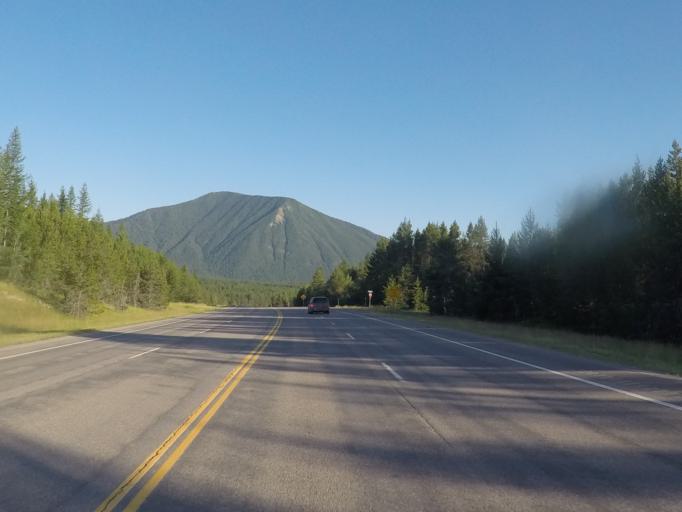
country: US
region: Montana
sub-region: Flathead County
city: Columbia Falls
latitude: 48.4766
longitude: -114.0011
